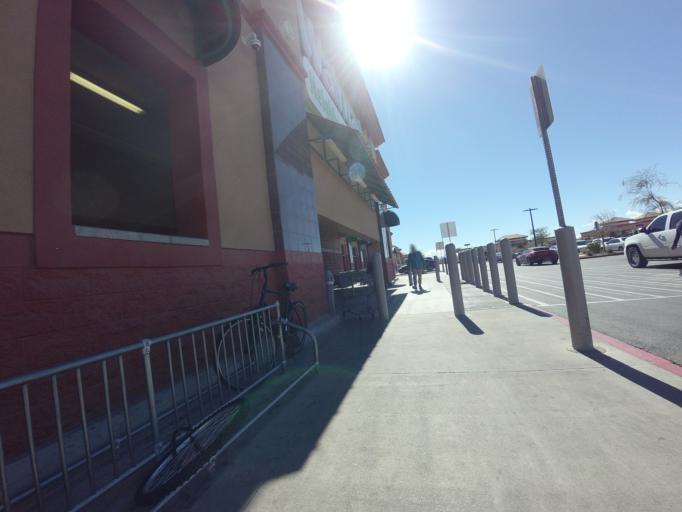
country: US
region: Nevada
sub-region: Clark County
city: Nellis Air Force Base
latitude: 36.2678
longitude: -115.1158
